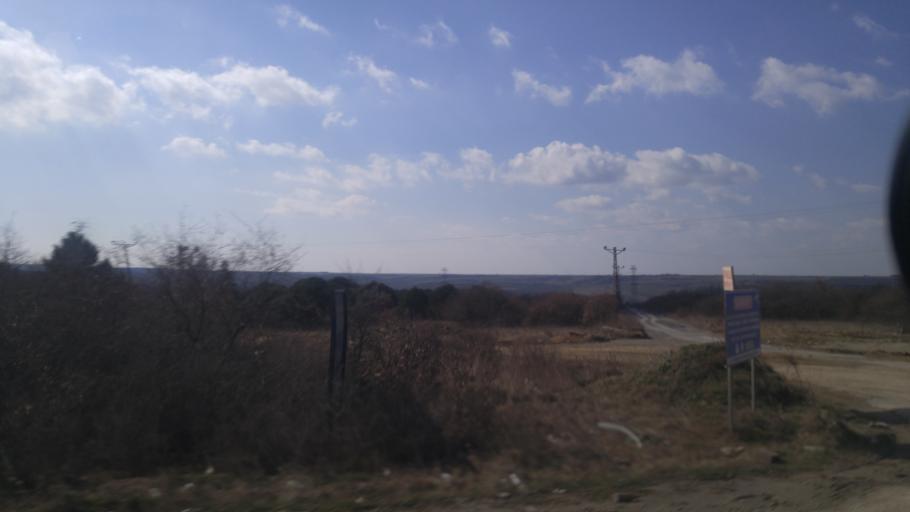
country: TR
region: Istanbul
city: Canta
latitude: 41.1803
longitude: 28.0880
